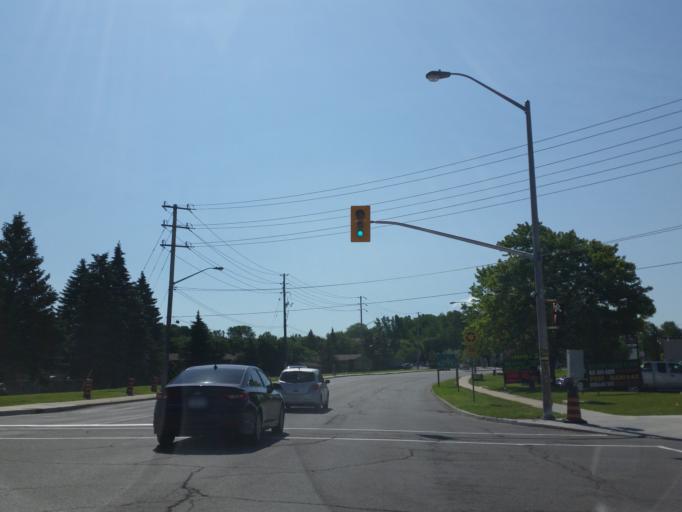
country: CA
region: Quebec
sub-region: Outaouais
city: Gatineau
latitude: 45.4662
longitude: -75.5426
